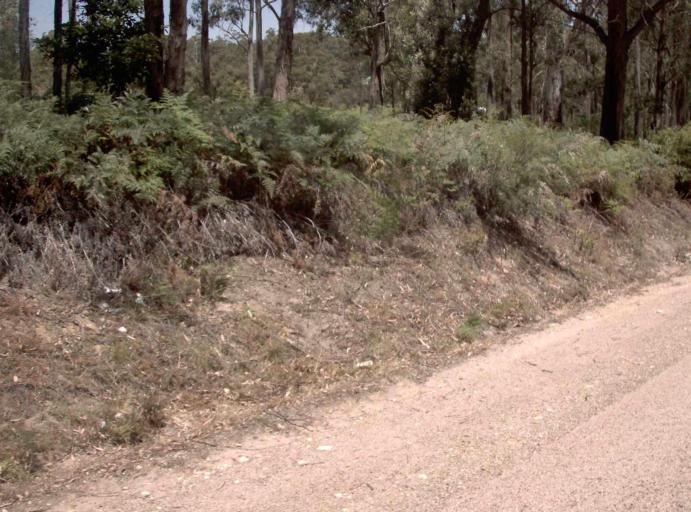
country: AU
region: Victoria
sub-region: East Gippsland
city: Bairnsdale
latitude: -37.7431
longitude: 147.7630
